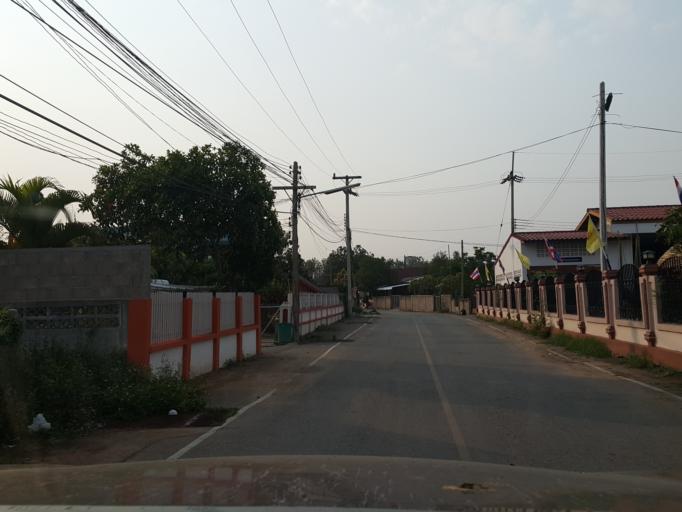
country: TH
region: Lamphun
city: Li
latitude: 17.8013
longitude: 98.9467
